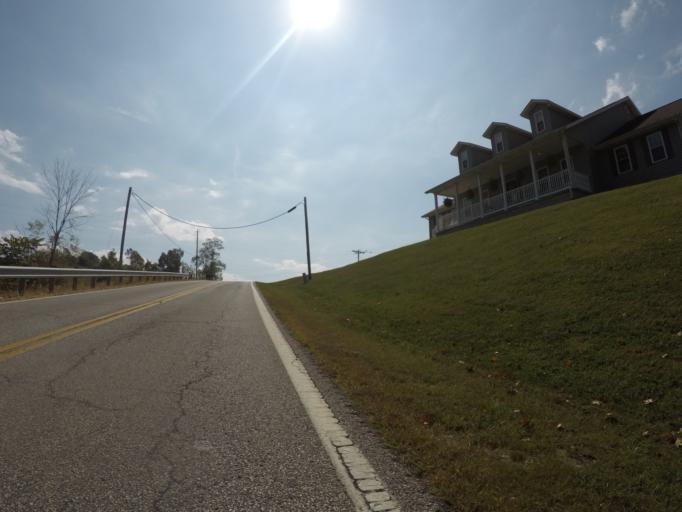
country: US
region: West Virginia
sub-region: Cabell County
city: Lesage
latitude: 38.5906
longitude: -82.4262
